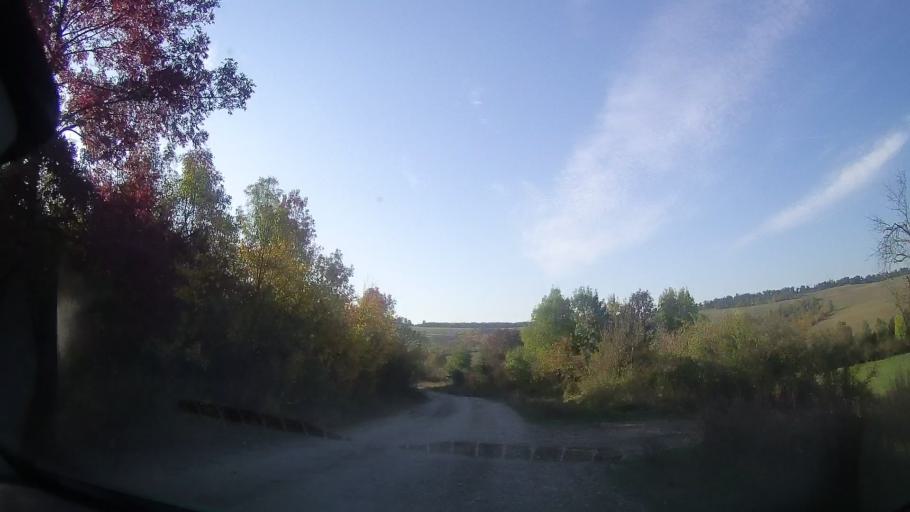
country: RO
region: Timis
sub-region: Comuna Bogda
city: Bogda
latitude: 45.9551
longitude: 21.6143
